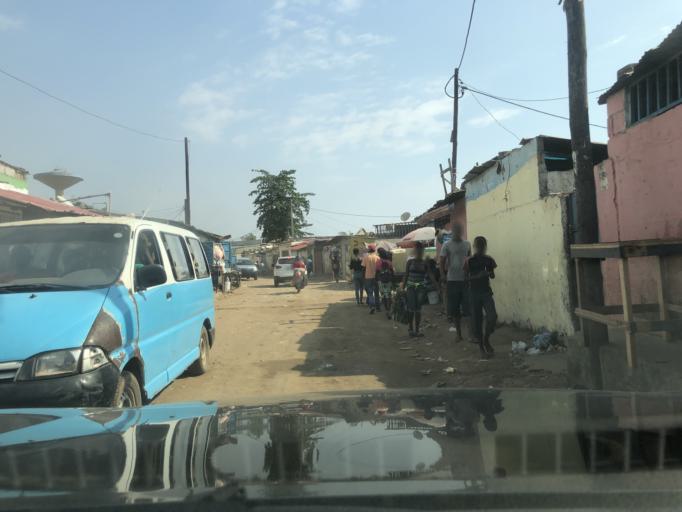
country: AO
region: Luanda
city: Luanda
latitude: -8.8527
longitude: 13.2550
